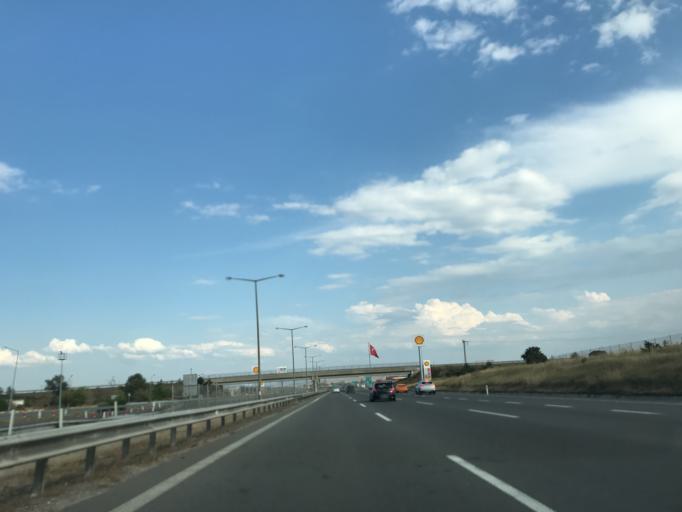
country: TR
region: Bolu
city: Dortdivan
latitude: 40.7520
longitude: 32.0777
